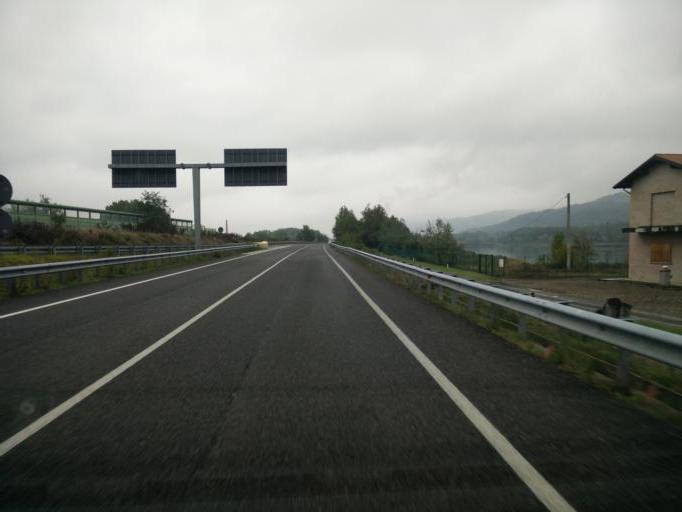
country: IT
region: Emilia-Romagna
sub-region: Provincia di Bologna
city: Borgonuovo
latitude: 44.4324
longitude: 11.2772
